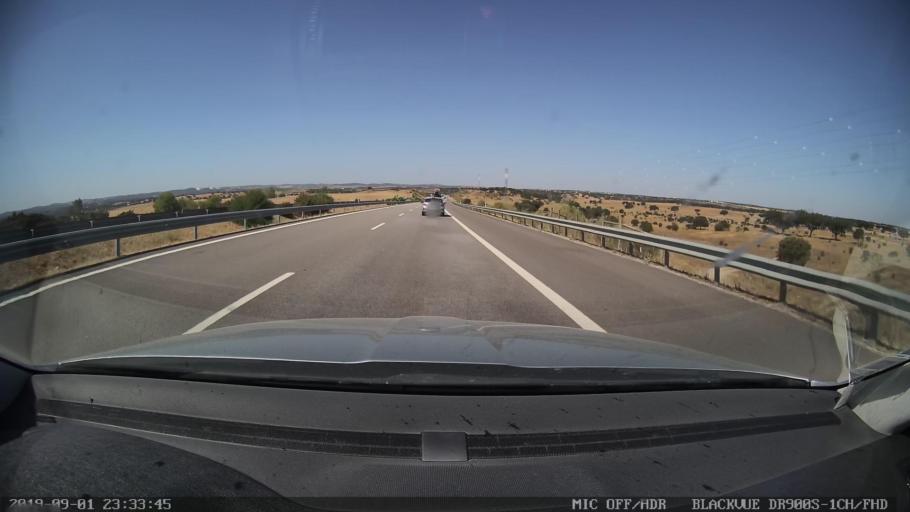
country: PT
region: Evora
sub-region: Vila Vicosa
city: Vila Vicosa
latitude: 38.8503
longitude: -7.3506
